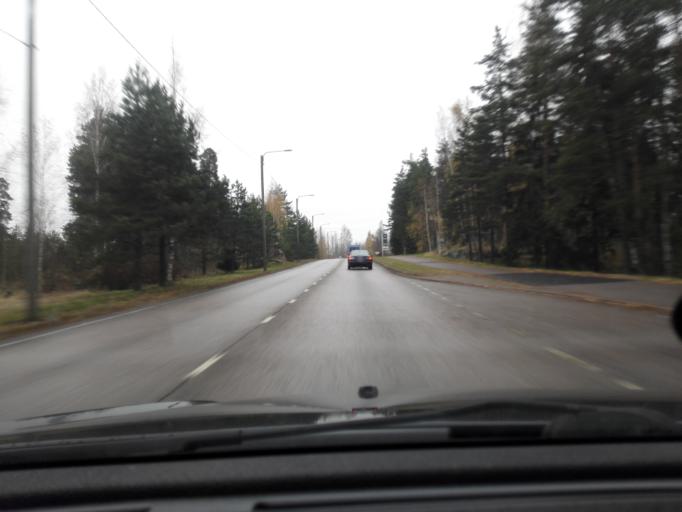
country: FI
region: Uusimaa
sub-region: Helsinki
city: Vantaa
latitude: 60.2969
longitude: 25.0855
